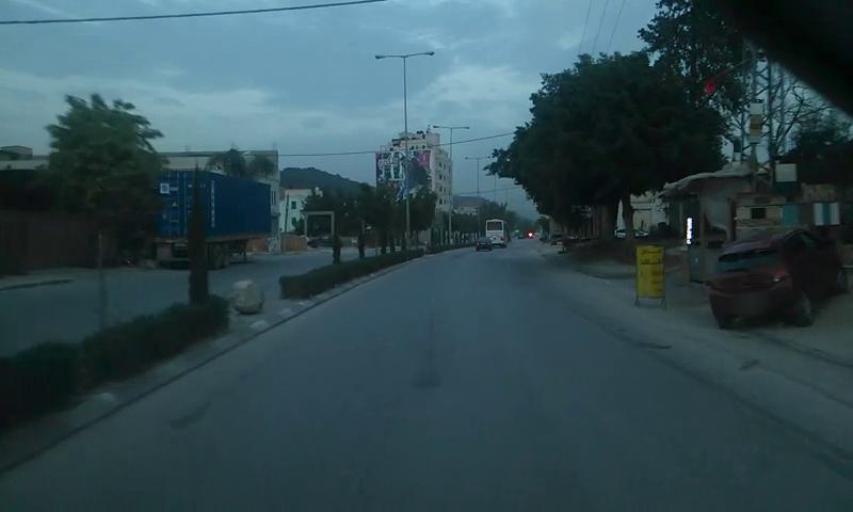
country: PS
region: West Bank
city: Iktabah
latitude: 32.3195
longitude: 35.0511
